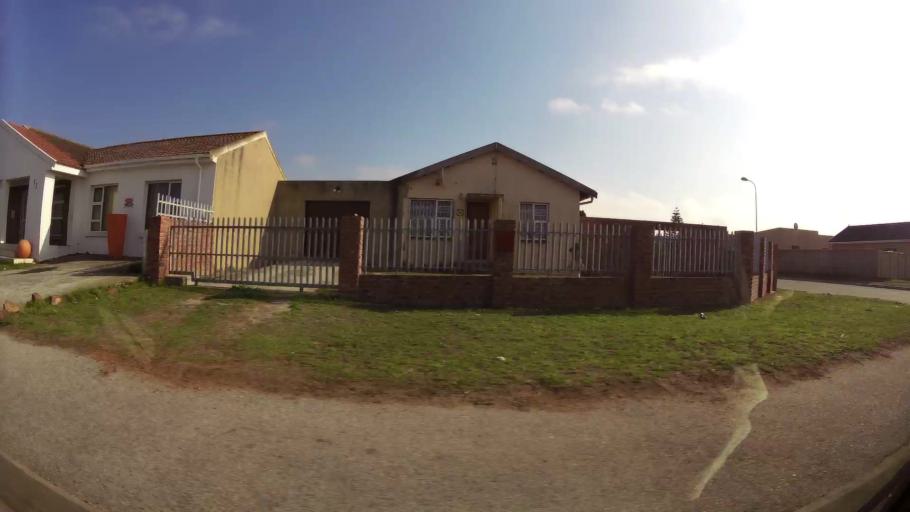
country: ZA
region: Eastern Cape
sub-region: Nelson Mandela Bay Metropolitan Municipality
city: Port Elizabeth
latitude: -33.9238
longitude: 25.5262
